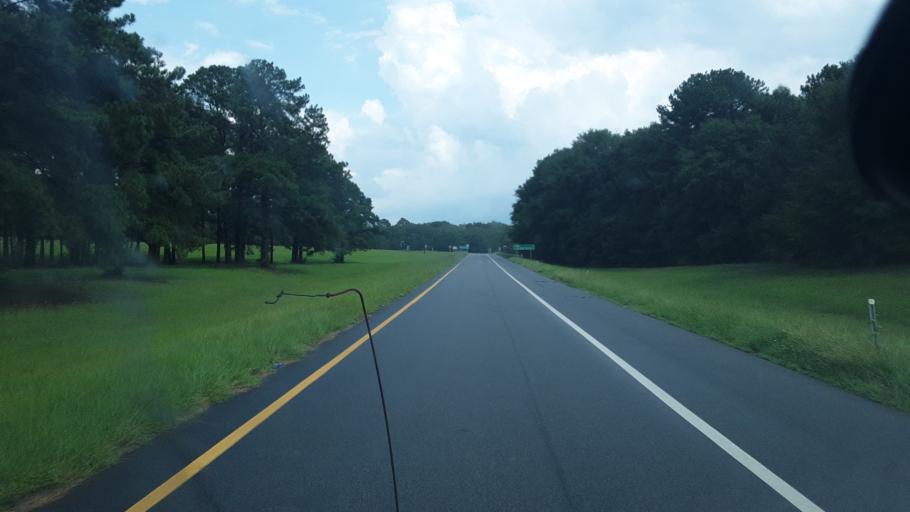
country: US
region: South Carolina
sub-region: Lee County
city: Bishopville
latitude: 34.1889
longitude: -80.1675
